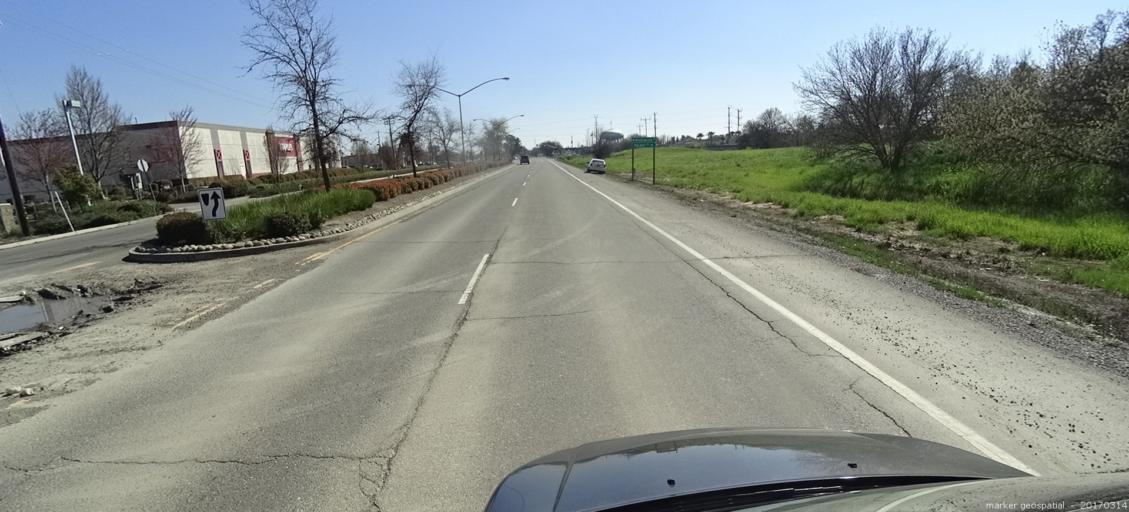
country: US
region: California
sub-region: Sacramento County
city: Parkway
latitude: 38.4836
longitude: -121.5055
